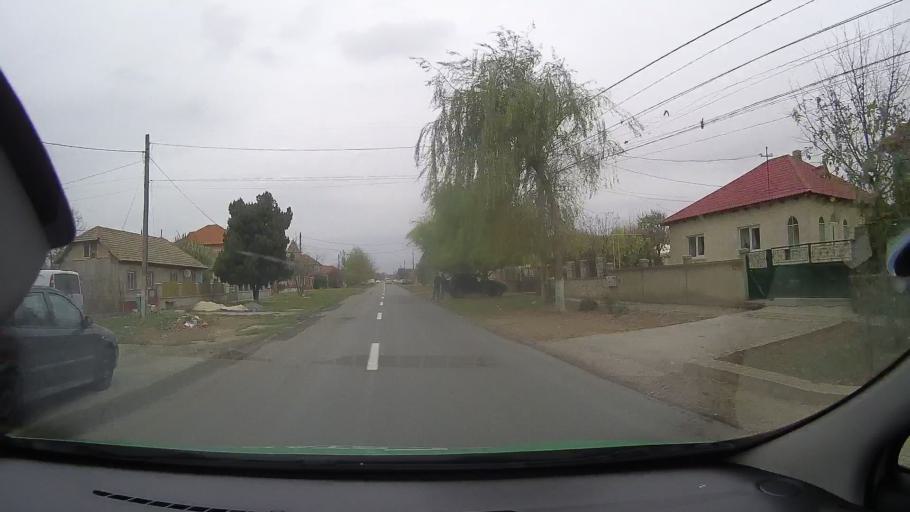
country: RO
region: Constanta
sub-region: Comuna Mihail Kogalniceanu
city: Mihail Kogalniceanu
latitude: 44.3744
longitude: 28.4645
